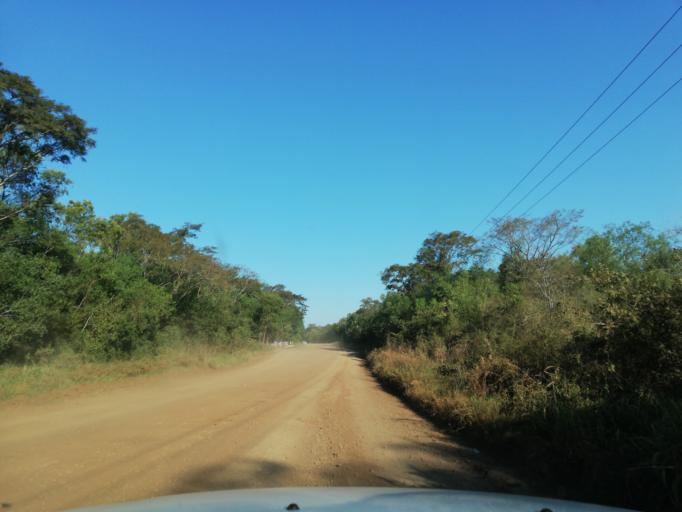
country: AR
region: Misiones
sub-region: Departamento de Candelaria
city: Candelaria
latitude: -27.5490
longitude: -55.7114
